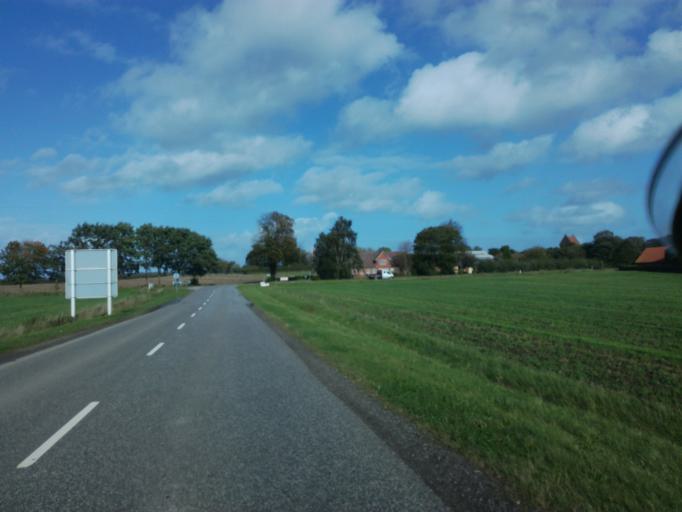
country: DK
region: South Denmark
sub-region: Vejle Kommune
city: Brejning
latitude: 55.6347
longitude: 9.6876
